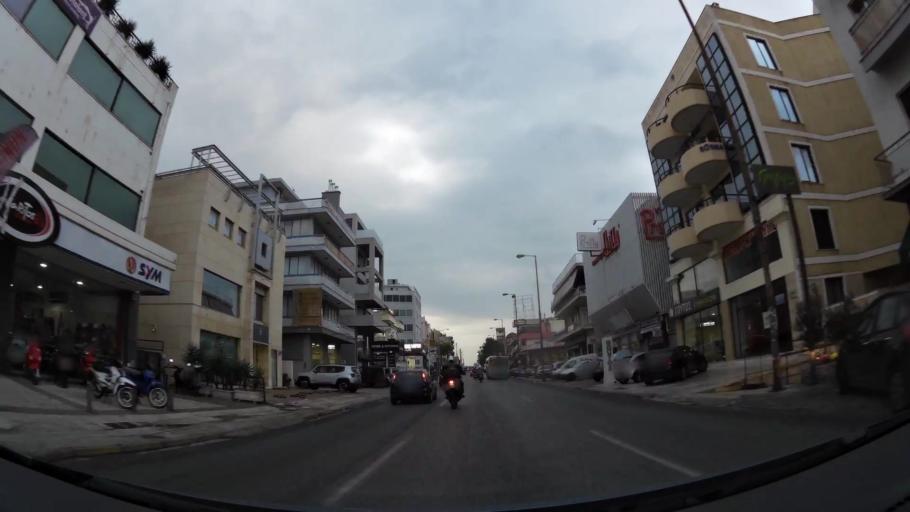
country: GR
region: Attica
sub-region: Nomarchia Athinas
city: Dhafni
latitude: 37.9463
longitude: 23.7390
